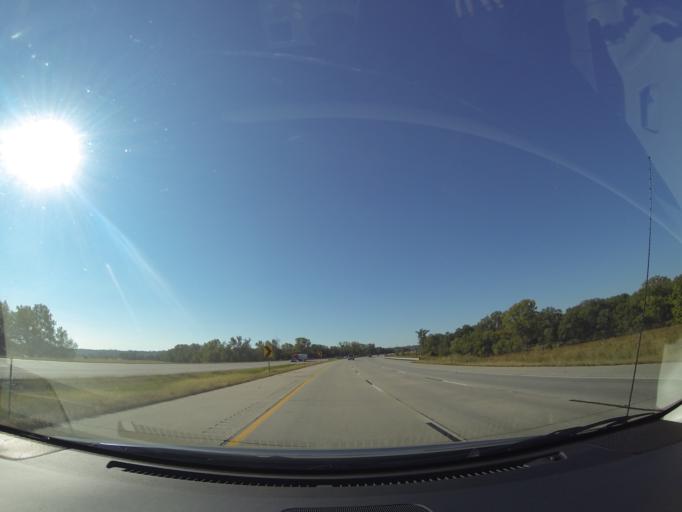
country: US
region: Nebraska
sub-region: Saunders County
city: Ashland
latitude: 41.0342
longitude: -96.2918
